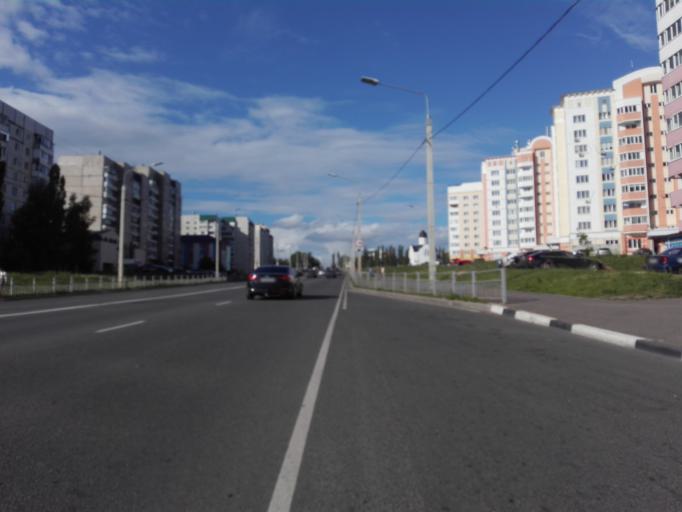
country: RU
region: Orjol
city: Orel
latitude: 53.0140
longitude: 36.1318
